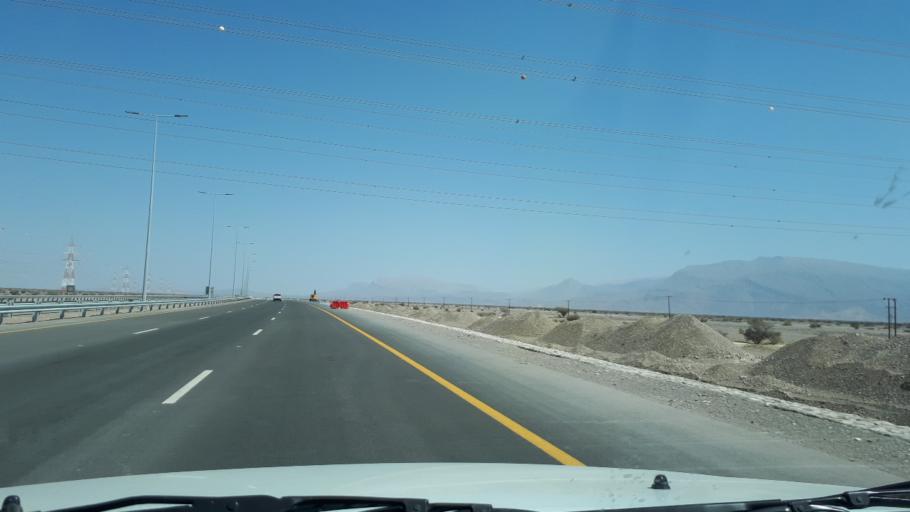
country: OM
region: Ash Sharqiyah
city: Badiyah
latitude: 22.3047
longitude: 59.1444
